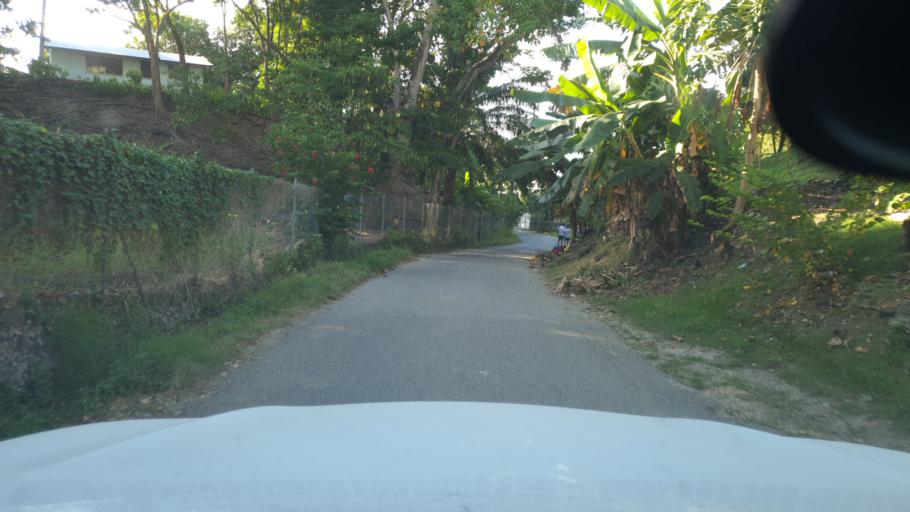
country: SB
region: Guadalcanal
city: Honiara
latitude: -9.4351
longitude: 159.9778
